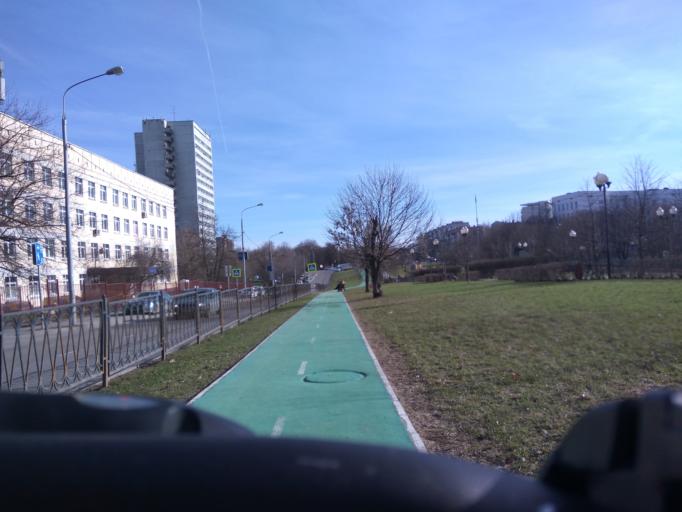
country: RU
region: Moscow
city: Davydkovo
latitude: 55.7221
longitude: 37.4618
